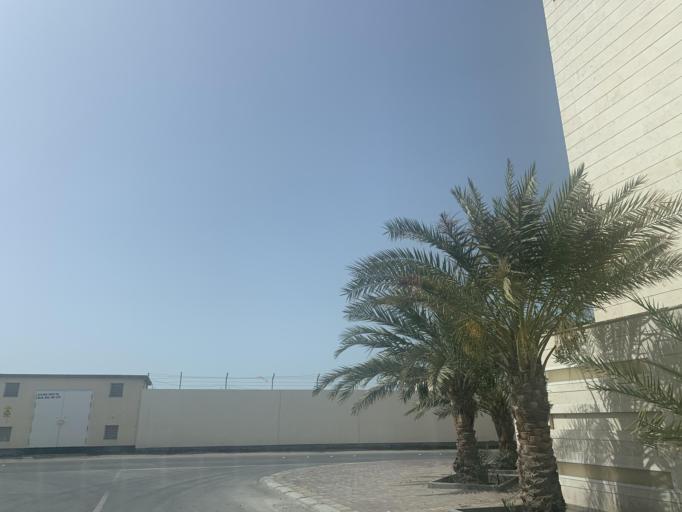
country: BH
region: Northern
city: Sitrah
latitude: 26.1653
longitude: 50.6190
